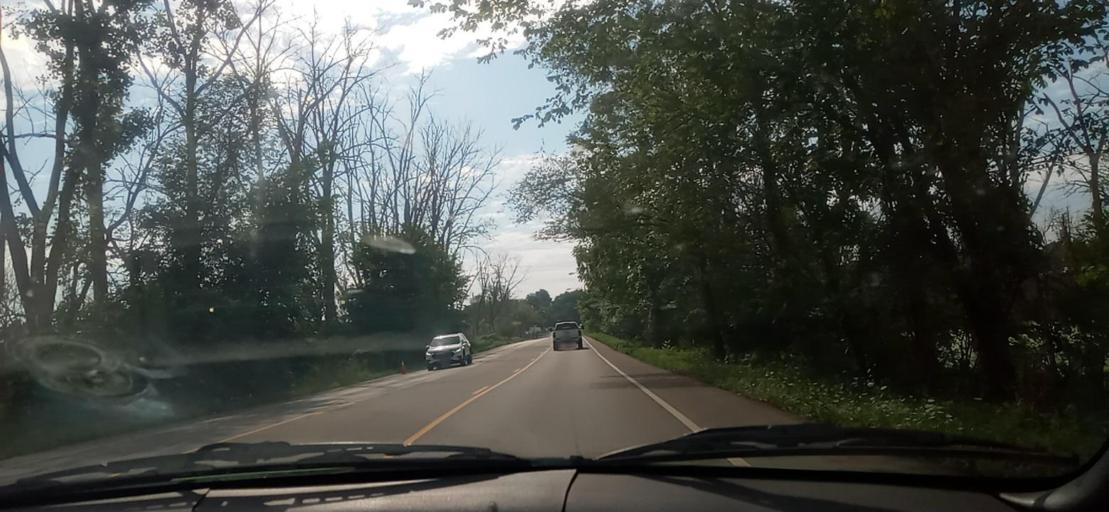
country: US
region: Ohio
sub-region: Summit County
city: Portage Lakes
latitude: 41.0288
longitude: -81.5326
